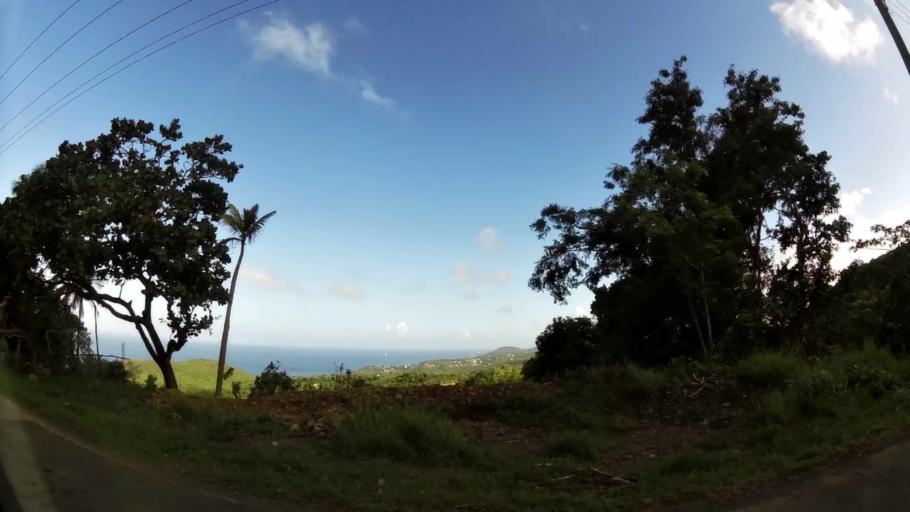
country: LC
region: Anse-la-Raye
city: Canaries
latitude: 13.9164
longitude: -61.0448
